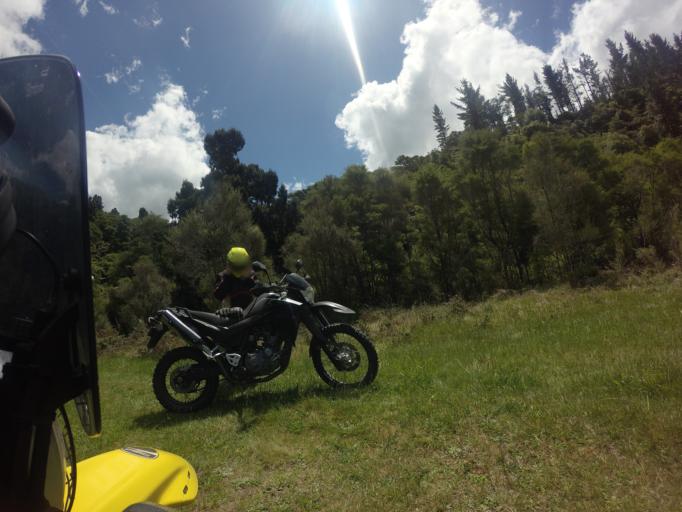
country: NZ
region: Hawke's Bay
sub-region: Wairoa District
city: Wairoa
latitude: -38.9658
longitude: 177.6644
